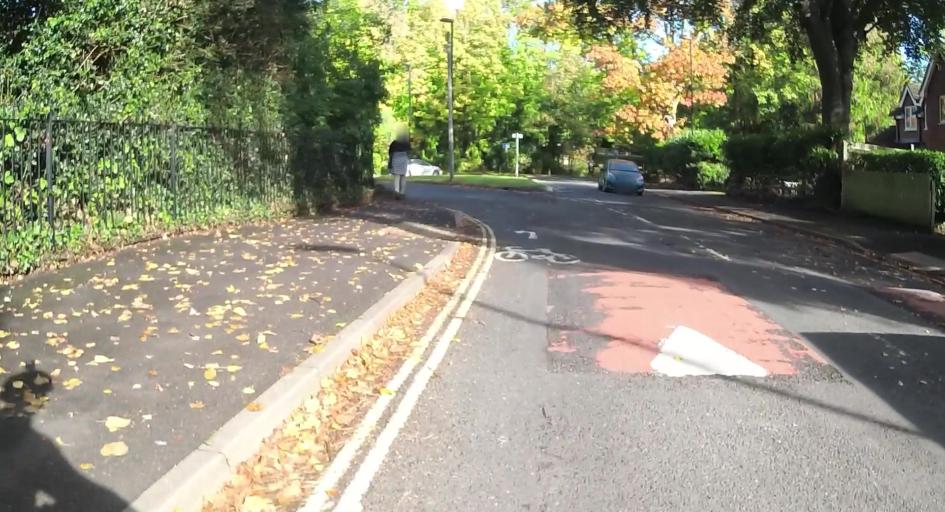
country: GB
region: England
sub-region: Hampshire
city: Basingstoke
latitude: 51.2565
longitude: -1.0854
